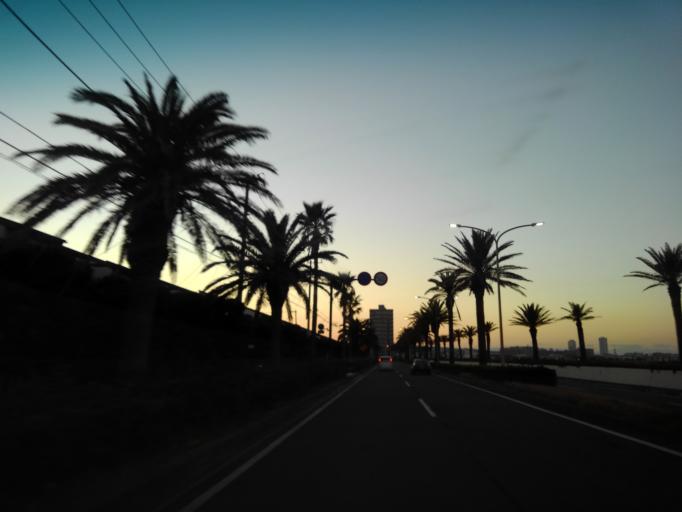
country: JP
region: Kanagawa
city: Yokosuka
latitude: 35.2637
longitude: 139.7024
